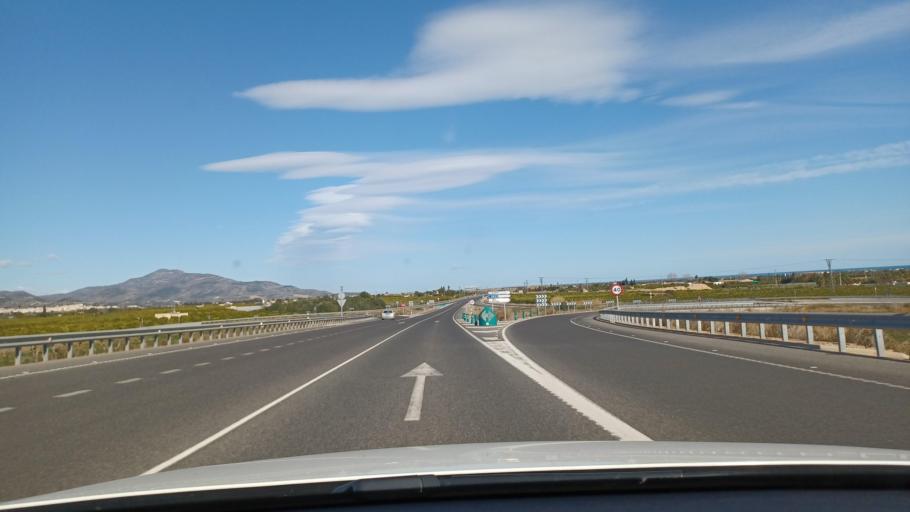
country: ES
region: Valencia
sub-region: Provincia de Castello
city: Vinaros
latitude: 40.4975
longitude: 0.4642
